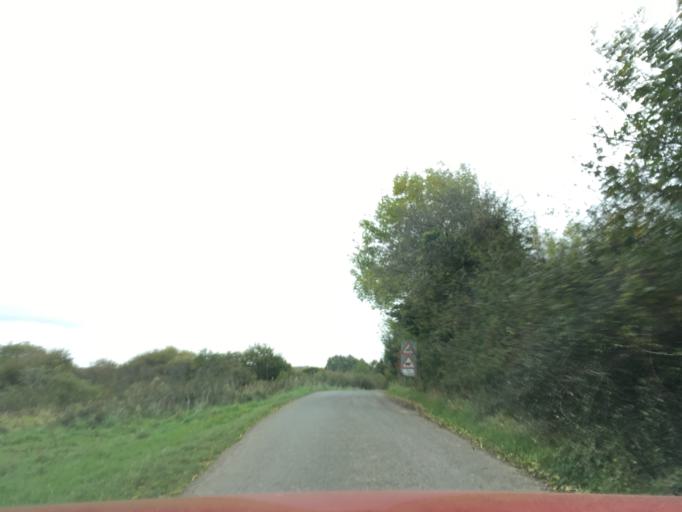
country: GB
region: England
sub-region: South Gloucestershire
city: Wickwar
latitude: 51.5970
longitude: -2.3729
